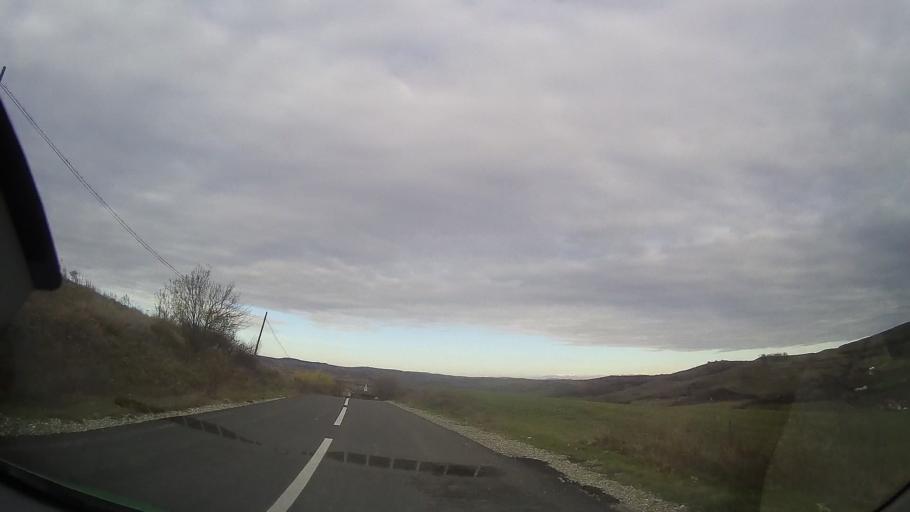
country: RO
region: Bistrita-Nasaud
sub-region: Comuna Micestii de Campie
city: Micestii de Campie
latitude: 46.8529
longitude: 24.3100
